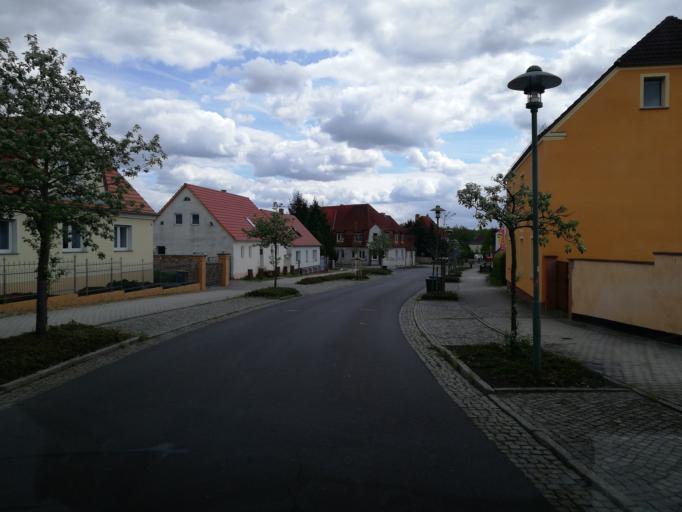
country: DE
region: Brandenburg
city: Lauchhammer
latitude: 51.4935
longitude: 13.7637
